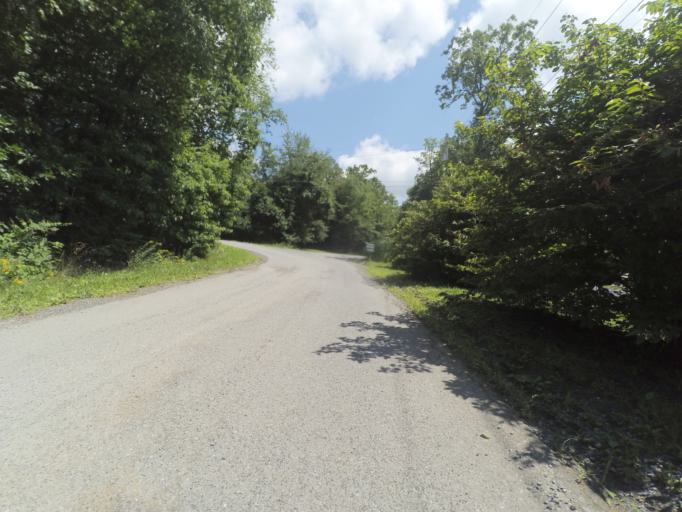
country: US
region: Pennsylvania
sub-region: Centre County
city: Stormstown
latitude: 40.7829
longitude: -78.0440
